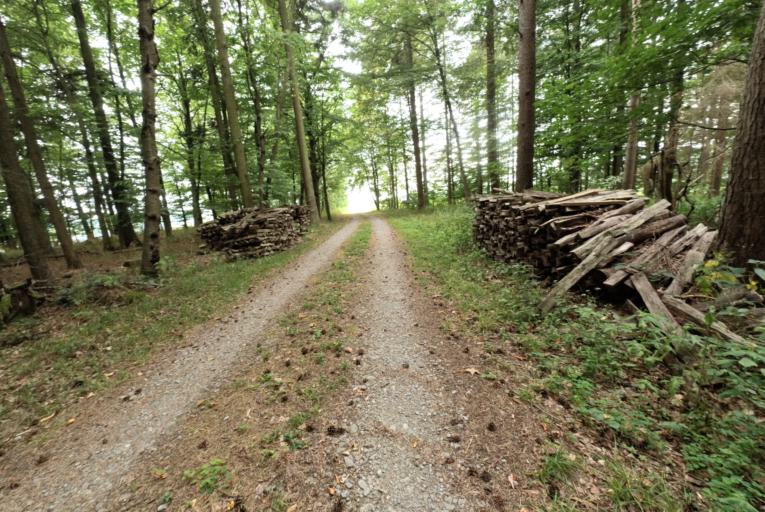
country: DE
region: Baden-Wuerttemberg
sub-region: Karlsruhe Region
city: Neckargerach
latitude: 49.3895
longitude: 9.0531
